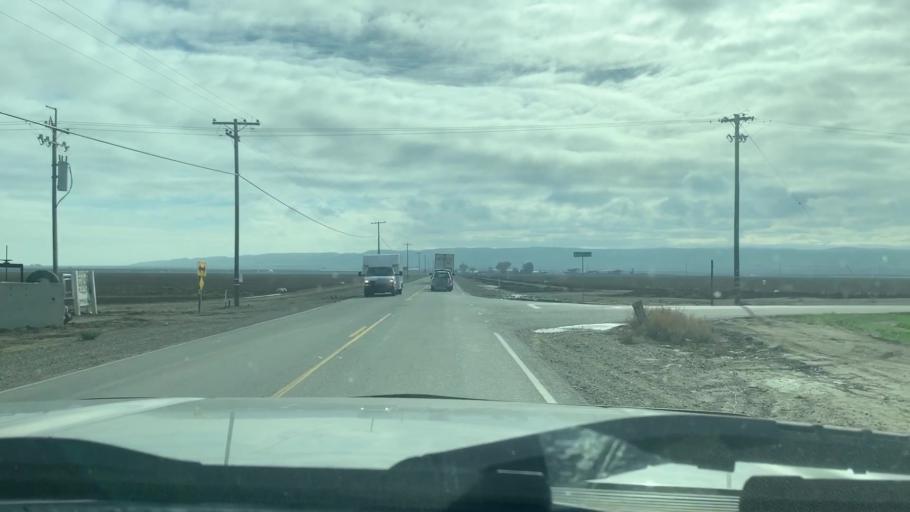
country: US
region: California
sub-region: Merced County
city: Los Banos
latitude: 36.9696
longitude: -120.8376
